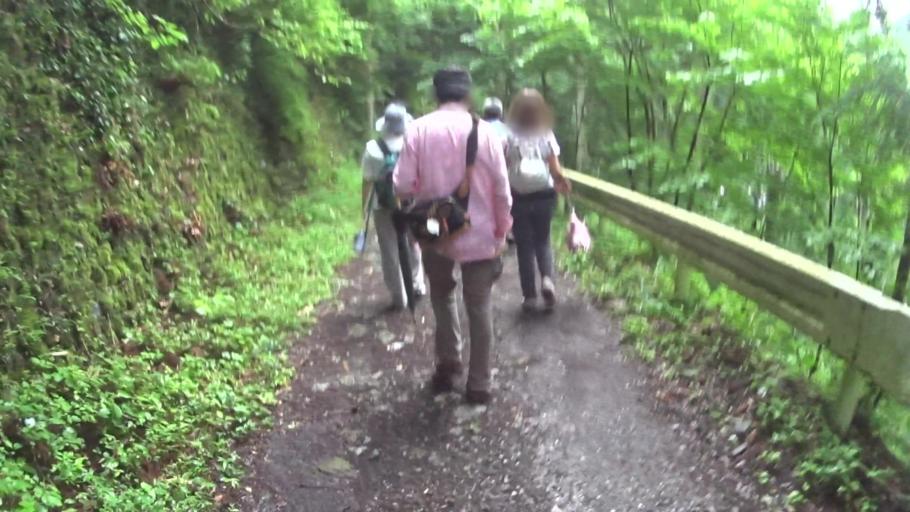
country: JP
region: Tokyo
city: Itsukaichi
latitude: 35.7979
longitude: 139.0778
